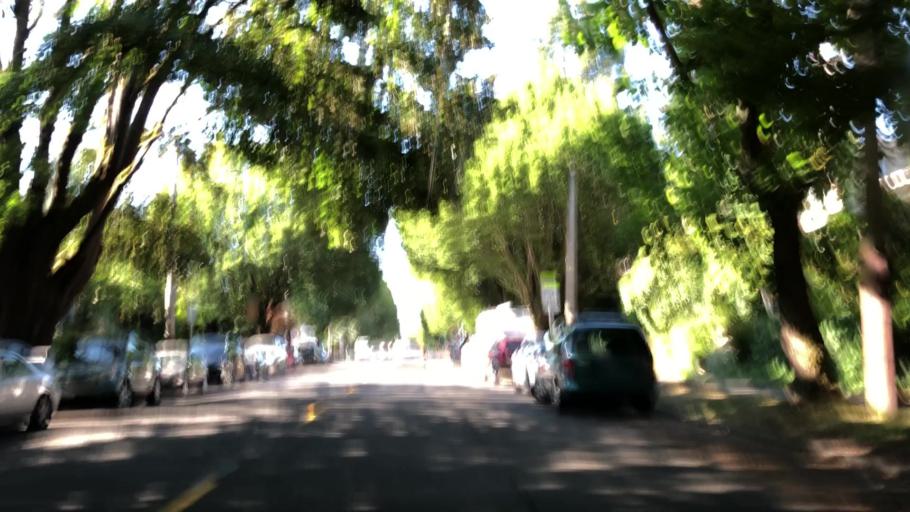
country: US
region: Washington
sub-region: King County
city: Seattle
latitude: 47.6279
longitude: -122.3073
